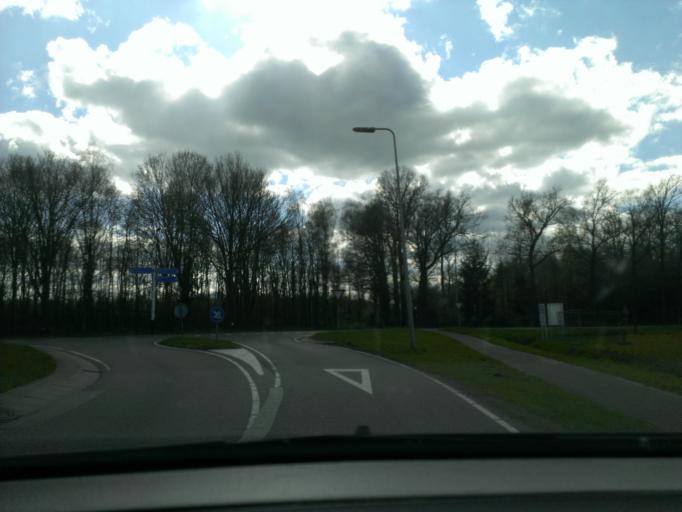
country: NL
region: Overijssel
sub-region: Gemeente Borne
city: Borne
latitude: 52.3127
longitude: 6.7024
